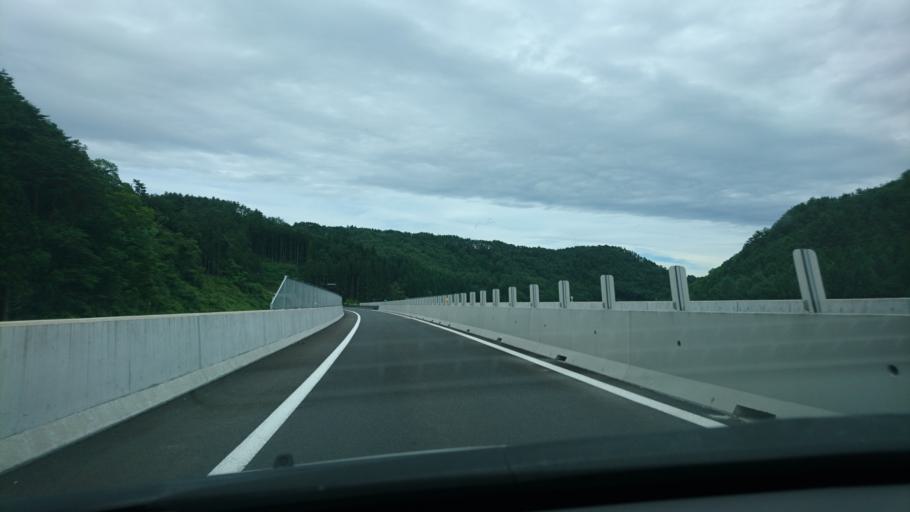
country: JP
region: Iwate
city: Miyako
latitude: 39.8212
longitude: 141.9622
